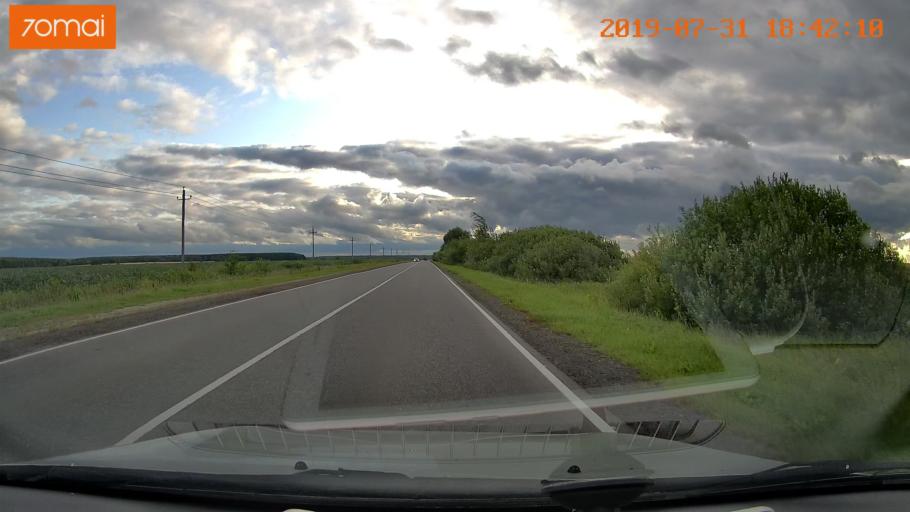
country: RU
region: Moskovskaya
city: Troitskoye
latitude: 55.2500
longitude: 38.5948
